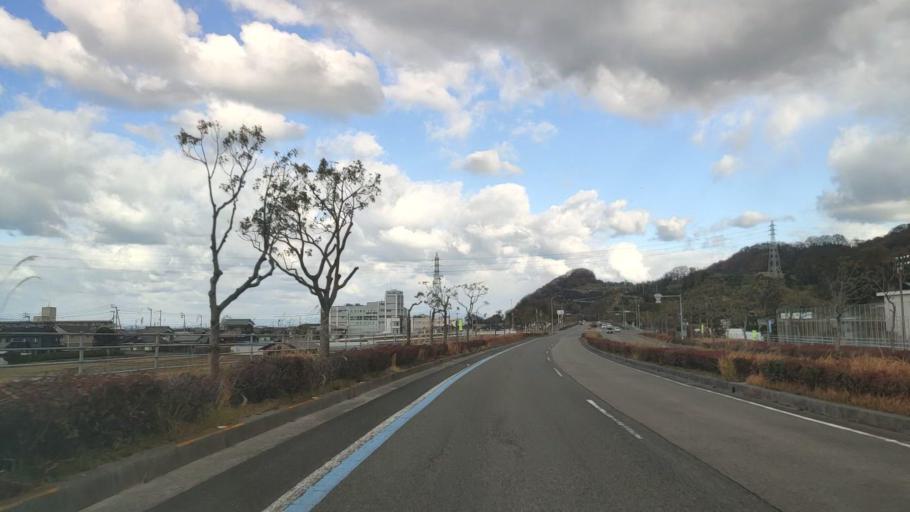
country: JP
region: Ehime
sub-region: Shikoku-chuo Shi
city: Matsuyama
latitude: 33.9008
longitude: 132.7570
